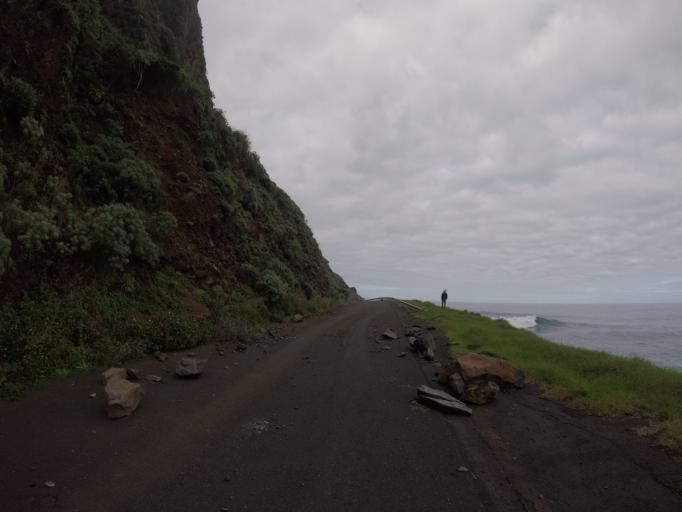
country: PT
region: Madeira
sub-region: Porto Moniz
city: Porto Moniz
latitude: 32.8508
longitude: -17.1502
